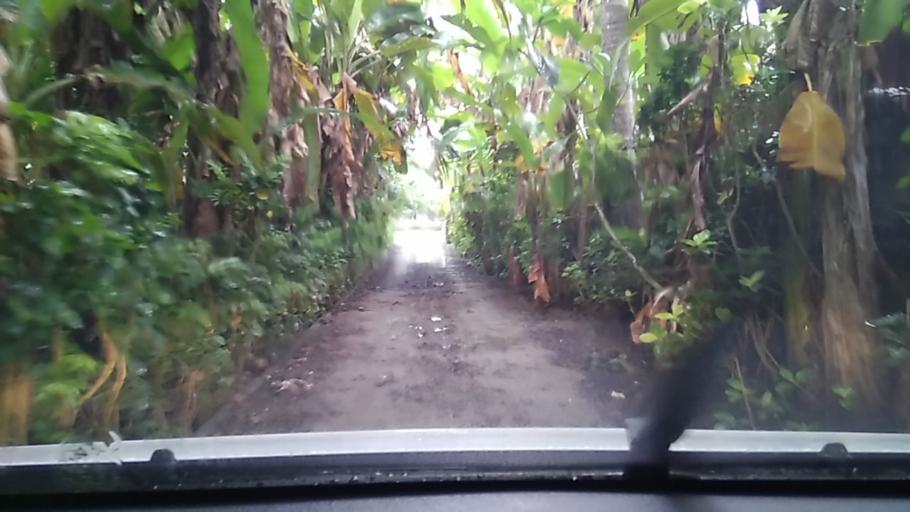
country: ID
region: Bali
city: Banjar Bugbug
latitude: -8.5131
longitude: 115.5773
